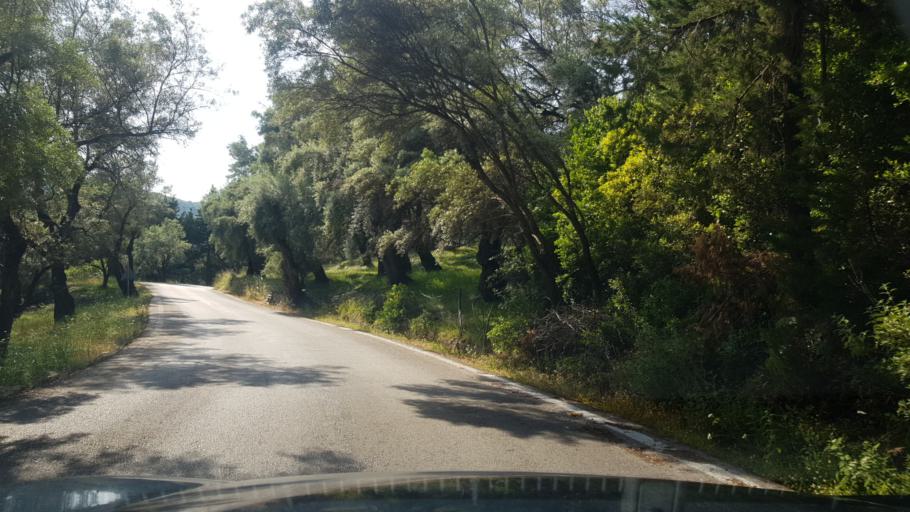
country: GR
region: Ionian Islands
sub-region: Lefkada
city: Nidri
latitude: 38.6534
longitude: 20.7048
